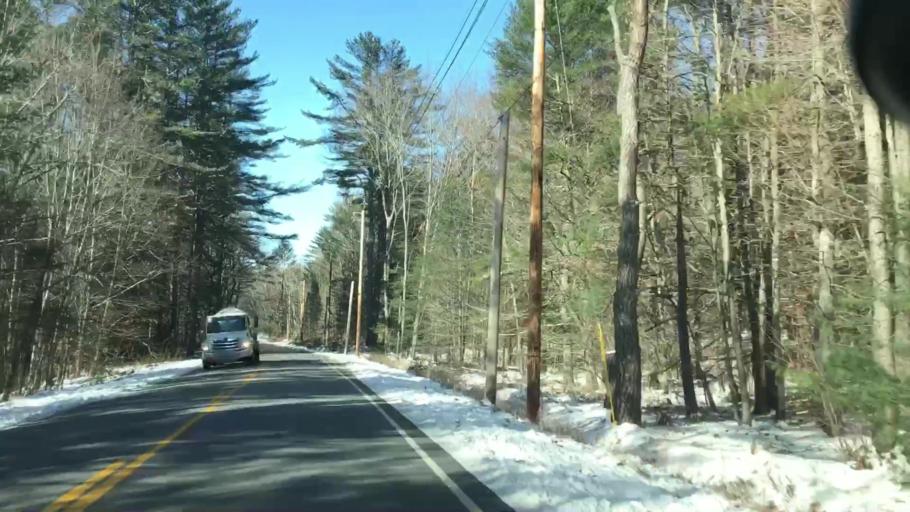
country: US
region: Maine
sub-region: Oxford County
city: Brownfield
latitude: 43.9641
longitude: -70.8649
